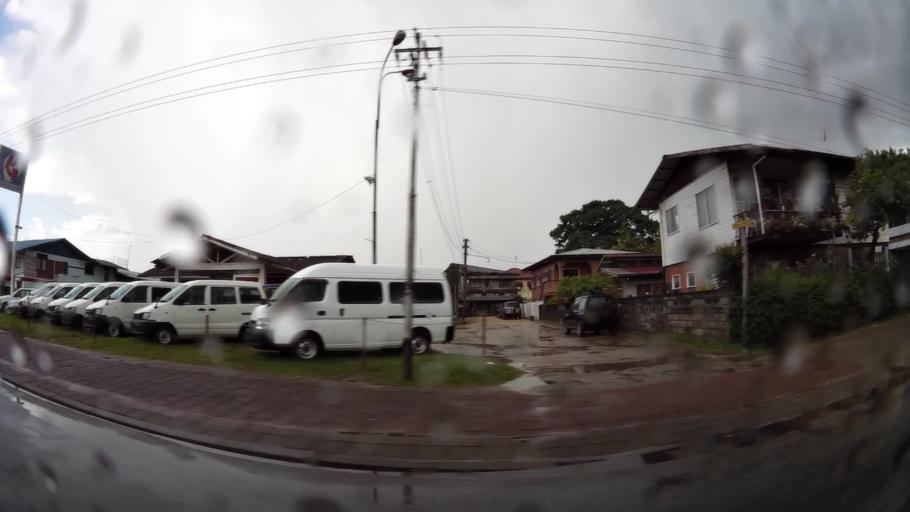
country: SR
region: Paramaribo
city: Paramaribo
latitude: 5.8182
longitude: -55.1752
